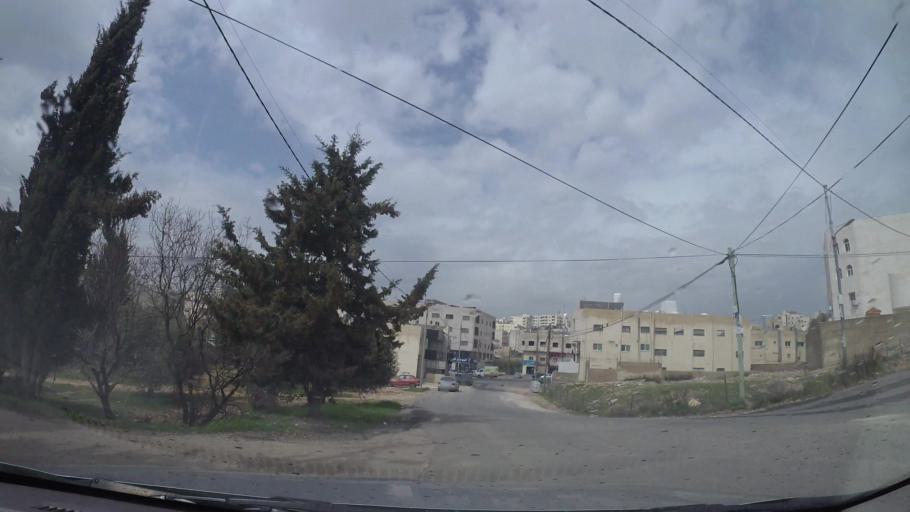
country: JO
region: Amman
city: Umm as Summaq
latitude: 31.9083
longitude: 35.8494
